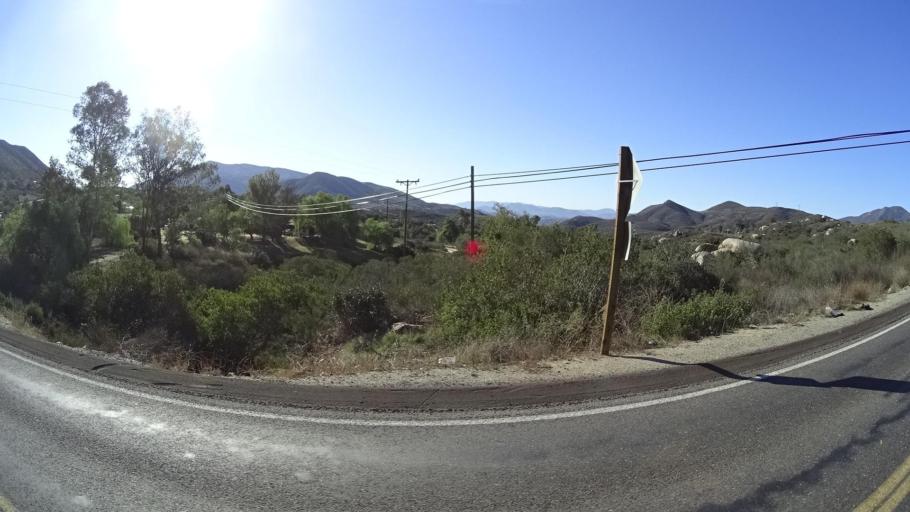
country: MX
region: Baja California
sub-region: Tijuana
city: Villa del Campo
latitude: 32.6242
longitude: -116.7543
